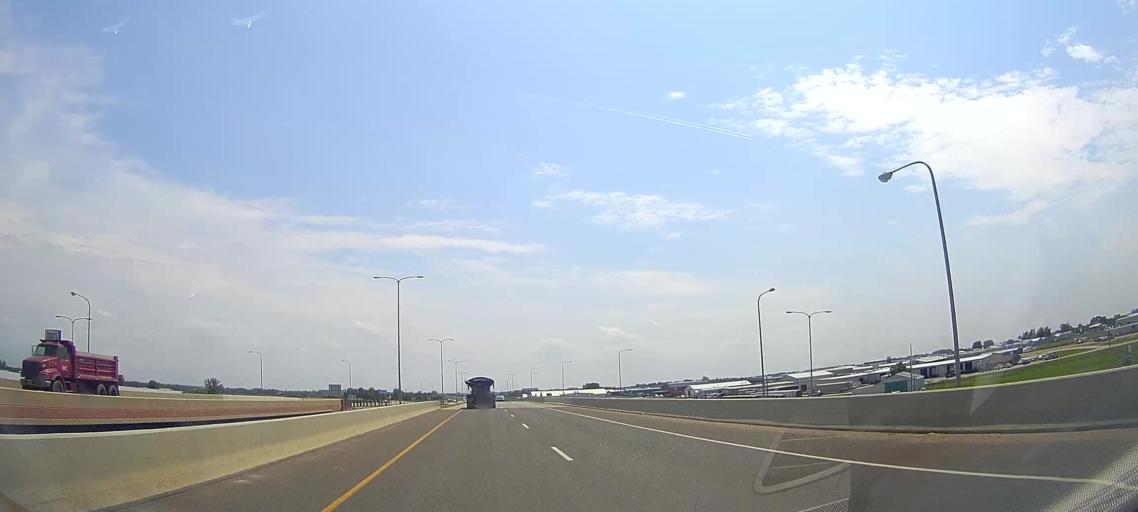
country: US
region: South Dakota
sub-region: Lincoln County
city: Tea
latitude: 43.4609
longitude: -96.7976
